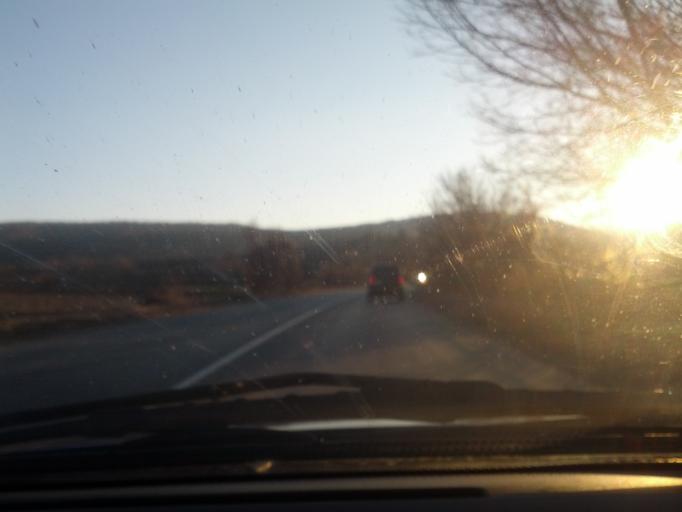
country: BG
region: Vratsa
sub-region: Obshtina Mezdra
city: Mezdra
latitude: 43.1257
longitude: 23.7085
